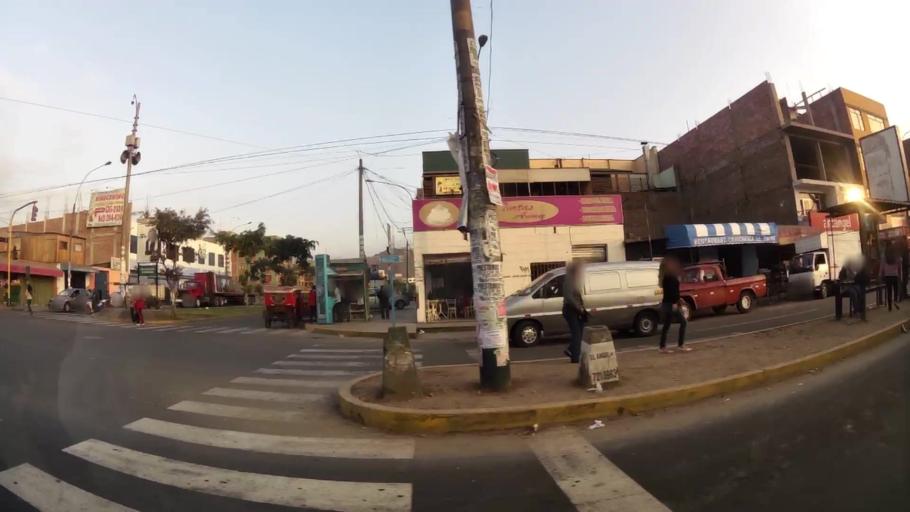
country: PE
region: Lima
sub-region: Lima
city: Independencia
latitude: -12.0060
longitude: -77.0715
